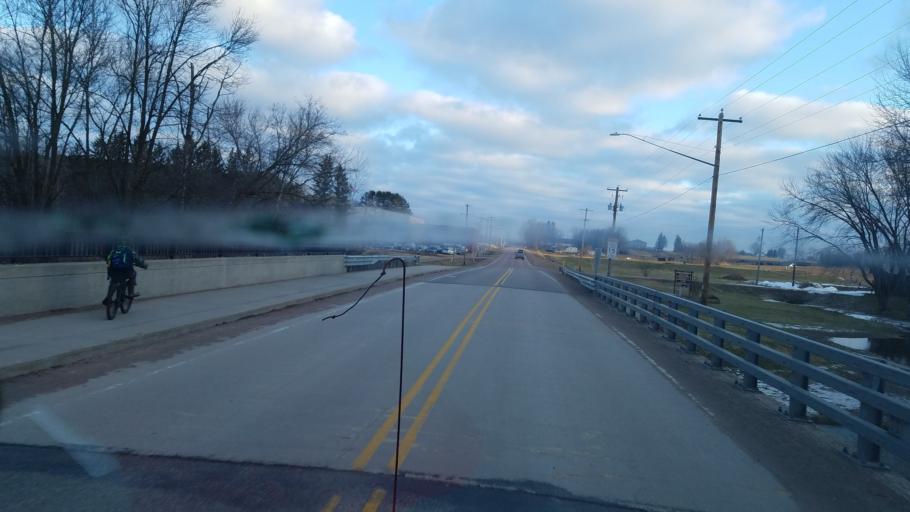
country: US
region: Wisconsin
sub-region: Clark County
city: Neillsville
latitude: 44.5901
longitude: -90.4615
